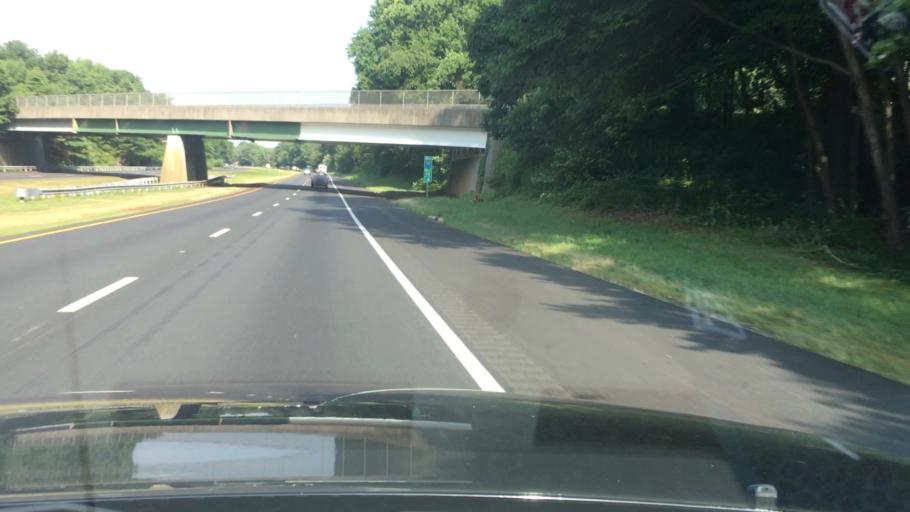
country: US
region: New Jersey
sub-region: Monmouth County
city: Shrewsbury
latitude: 40.1742
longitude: -74.4625
